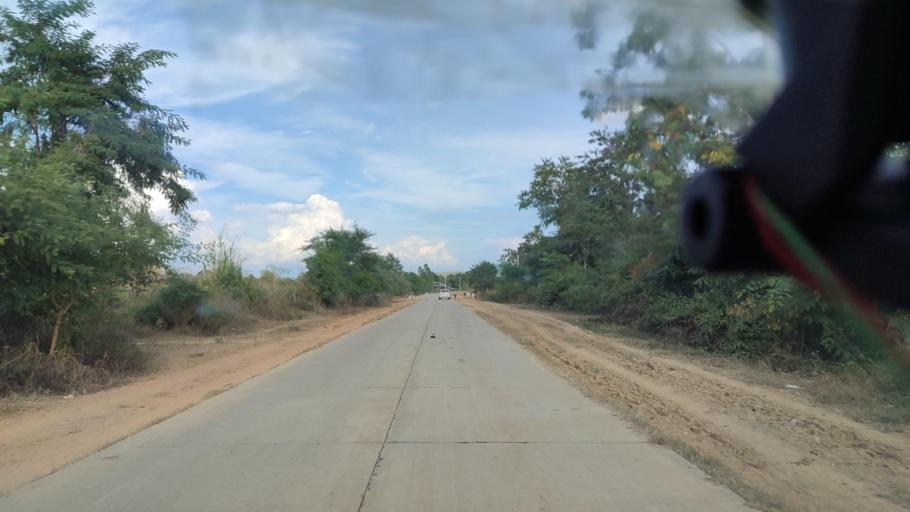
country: MM
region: Mandalay
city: Yamethin
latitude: 20.1002
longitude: 95.9911
